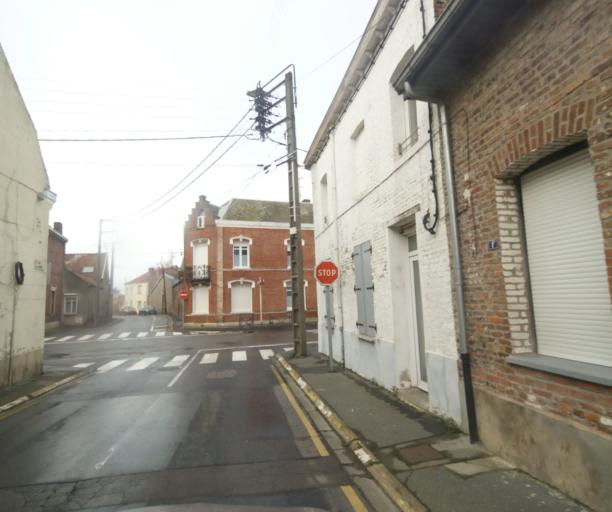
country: FR
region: Nord-Pas-de-Calais
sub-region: Departement du Nord
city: Famars
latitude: 50.3144
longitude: 3.5191
